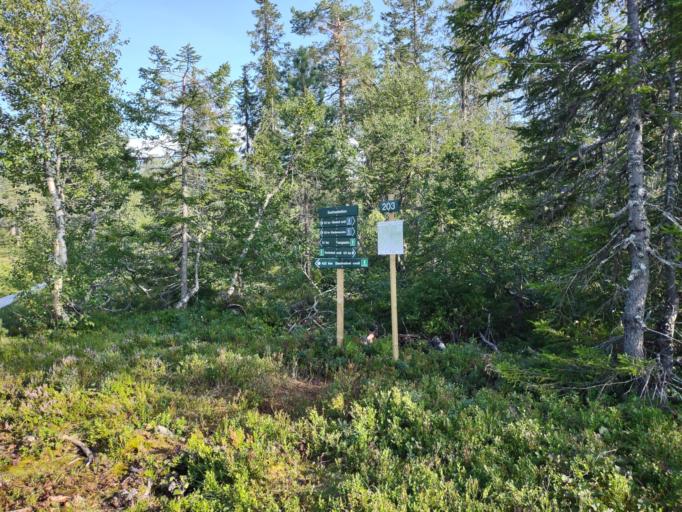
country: NO
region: Buskerud
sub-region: Rollag
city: Rollag
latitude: 59.8253
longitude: 9.3281
